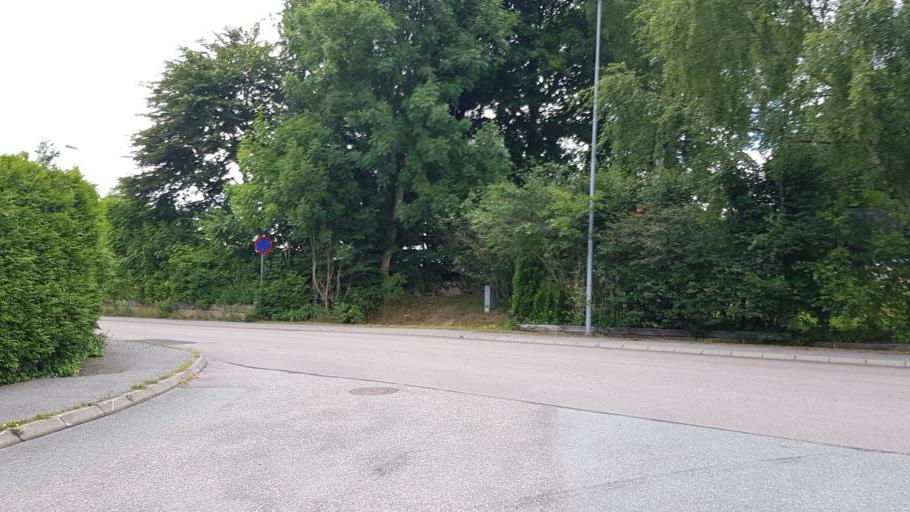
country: SE
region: Vaestra Goetaland
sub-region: Partille Kommun
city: Furulund
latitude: 57.7016
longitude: 12.1354
